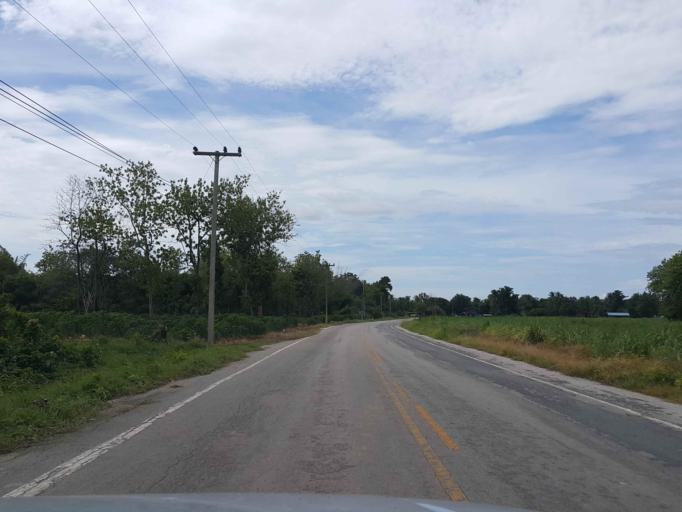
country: TH
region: Sukhothai
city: Ban Dan Lan Hoi
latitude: 17.0815
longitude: 99.4790
